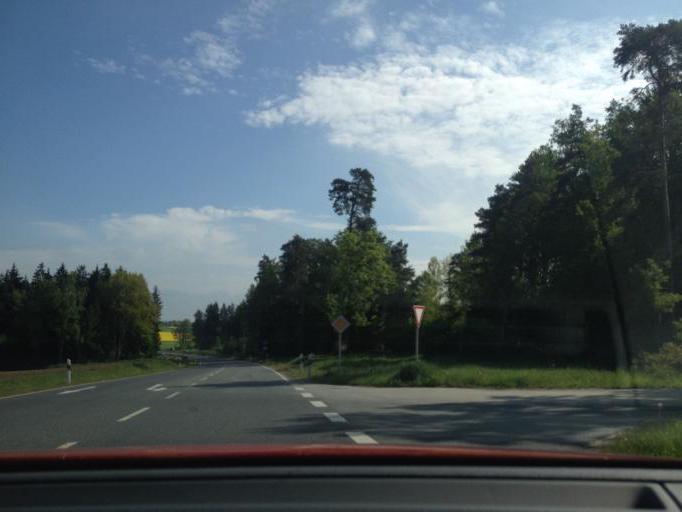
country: DE
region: Bavaria
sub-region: Upper Palatinate
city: Waldershof
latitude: 49.9620
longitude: 12.0368
